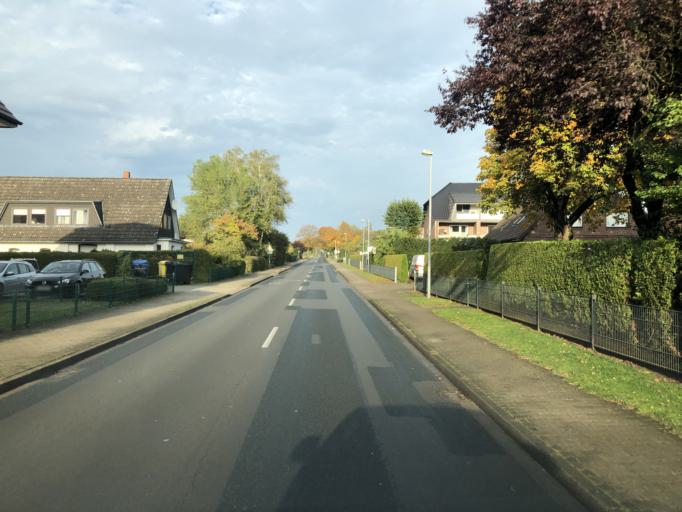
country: DE
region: Lower Saxony
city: Neu Wulmstorf
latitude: 53.4273
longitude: 9.7912
